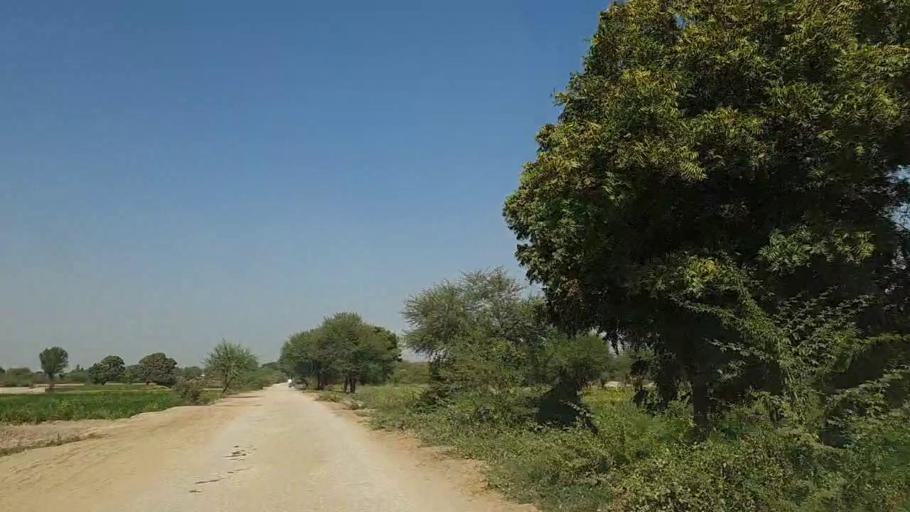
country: PK
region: Sindh
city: Naukot
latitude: 24.8708
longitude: 69.4037
